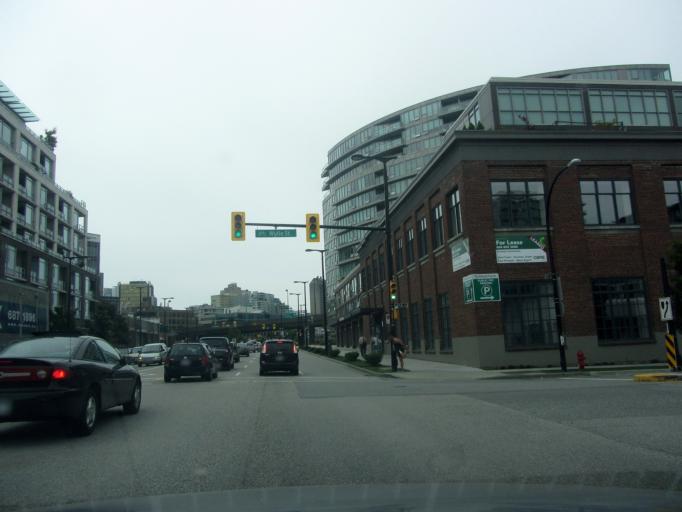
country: CA
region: British Columbia
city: Vancouver
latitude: 49.2680
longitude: -123.1007
